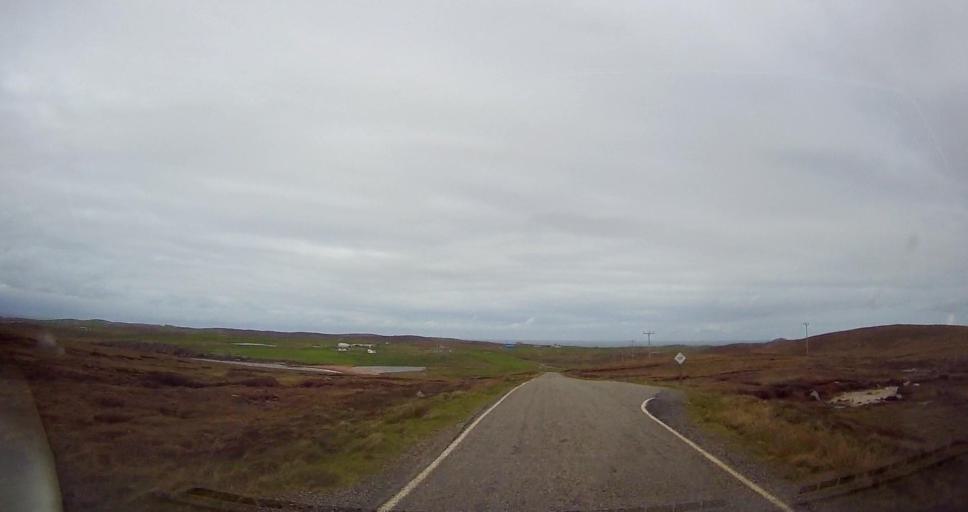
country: GB
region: Scotland
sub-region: Shetland Islands
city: Lerwick
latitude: 60.4870
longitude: -1.5348
